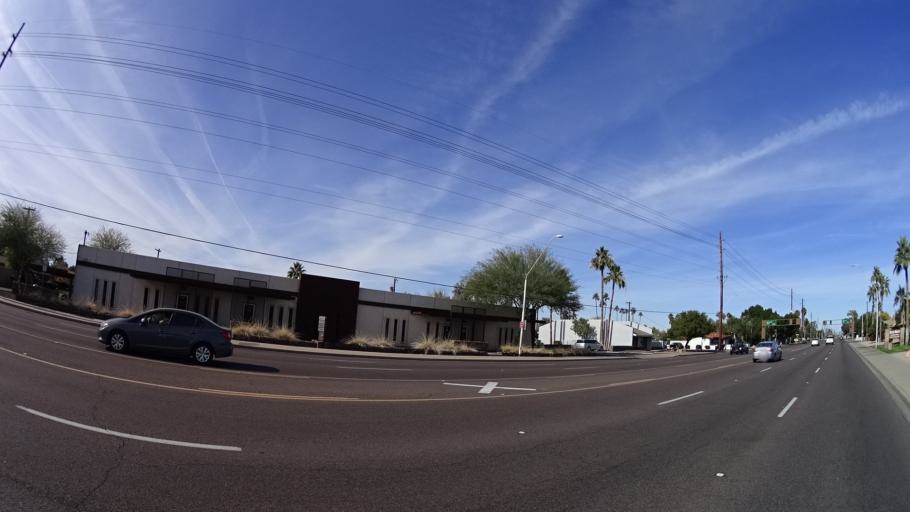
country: US
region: Arizona
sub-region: Maricopa County
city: Tempe Junction
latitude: 33.3989
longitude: -111.9262
